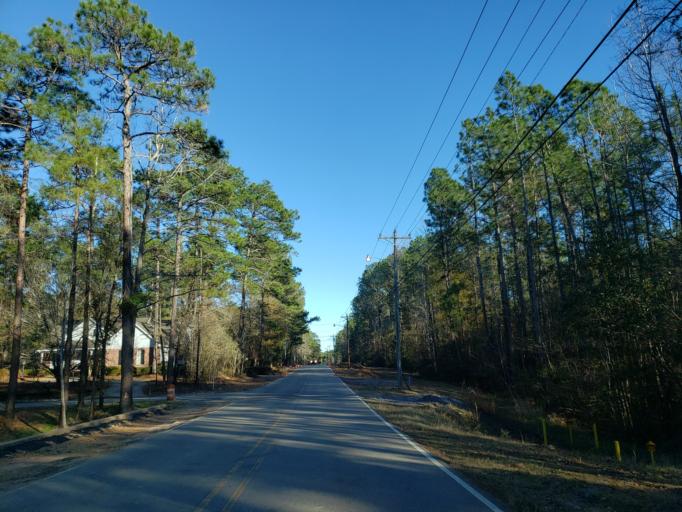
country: US
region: Mississippi
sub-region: Lamar County
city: Arnold Line
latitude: 31.3467
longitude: -89.3814
